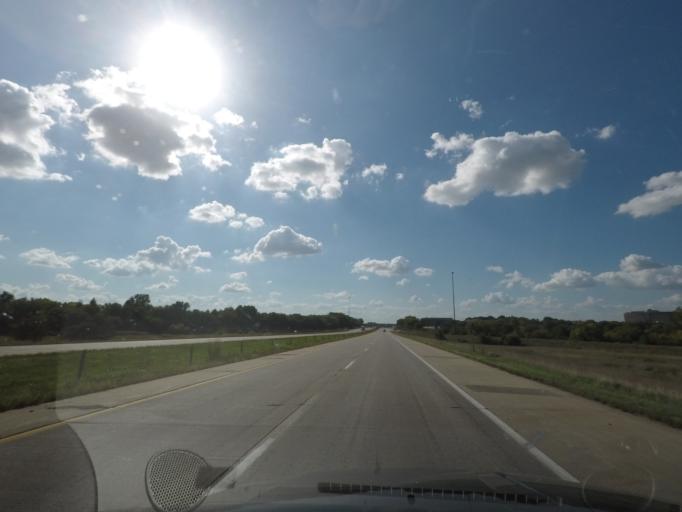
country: US
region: Iowa
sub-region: Polk County
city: Clive
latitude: 41.5923
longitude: -93.7804
